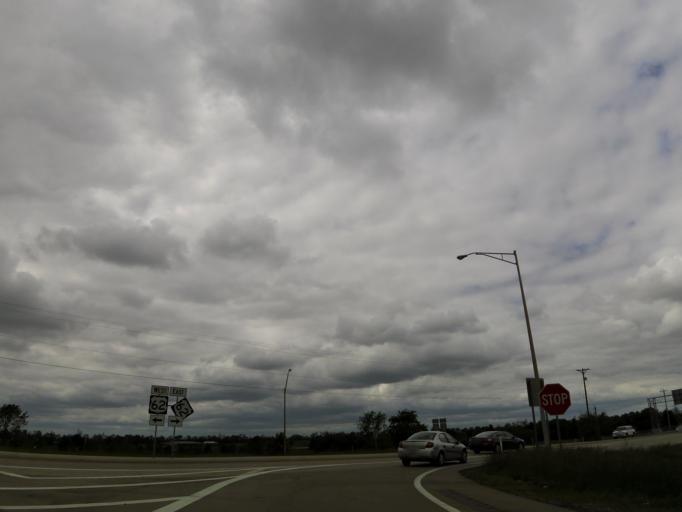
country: US
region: Kentucky
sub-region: Woodford County
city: Midway
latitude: 38.1590
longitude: -84.6113
